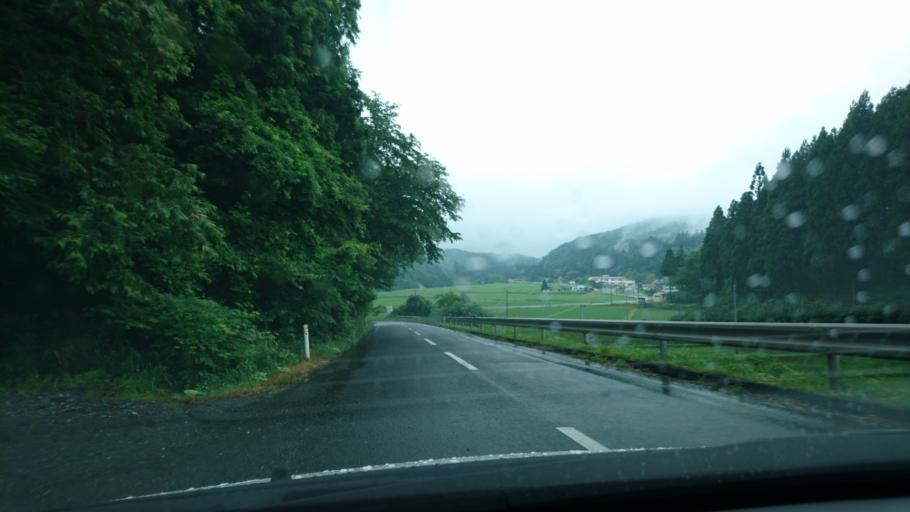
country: JP
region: Iwate
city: Ichinoseki
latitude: 38.9042
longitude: 141.0311
